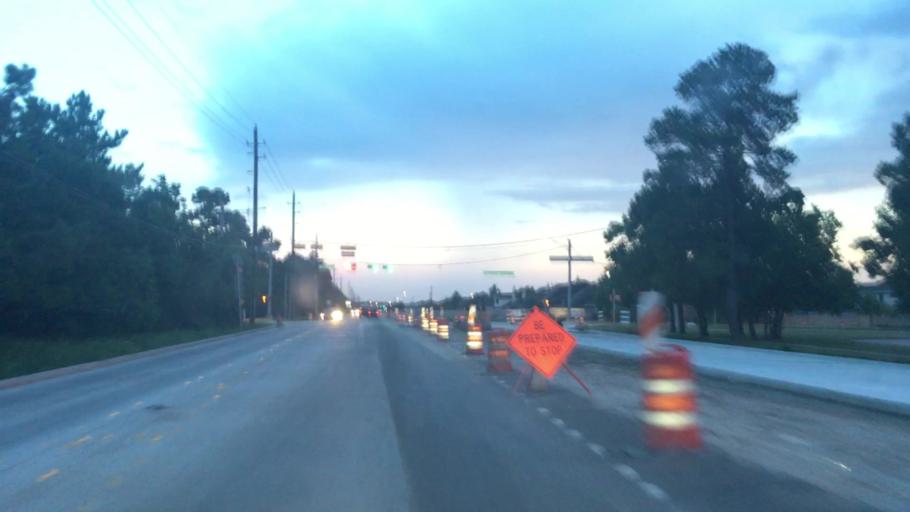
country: US
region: Texas
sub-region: Harris County
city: Humble
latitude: 29.9442
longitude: -95.2497
